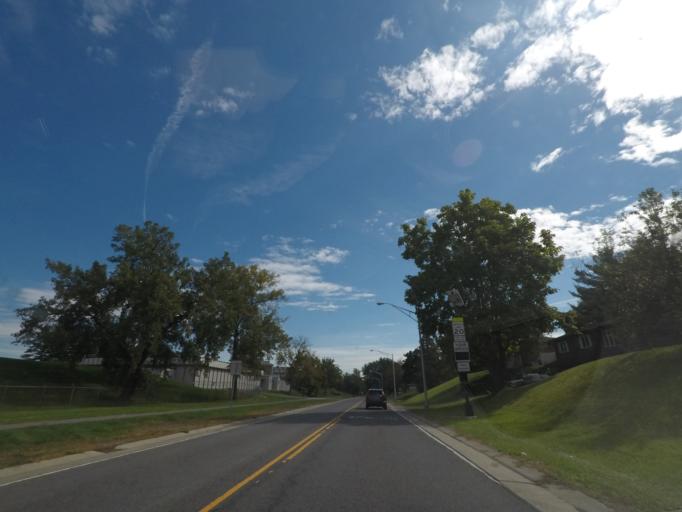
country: US
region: New York
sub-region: Albany County
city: Albany
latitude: 42.6467
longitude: -73.7909
